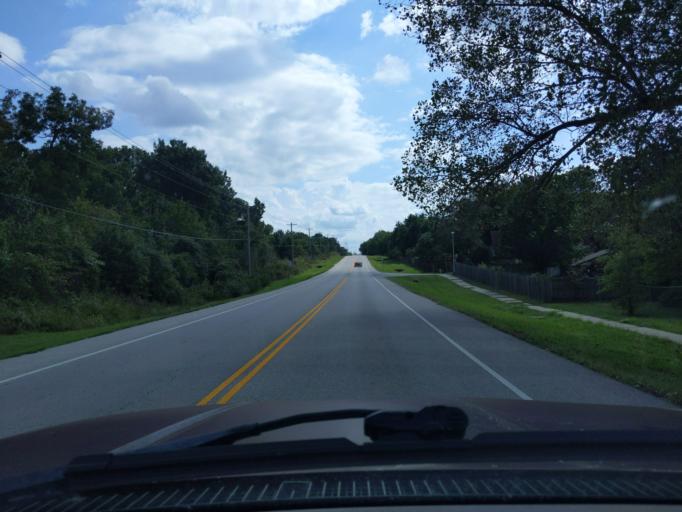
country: US
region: Oklahoma
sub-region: Tulsa County
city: Oakhurst
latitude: 36.0719
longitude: -96.0117
